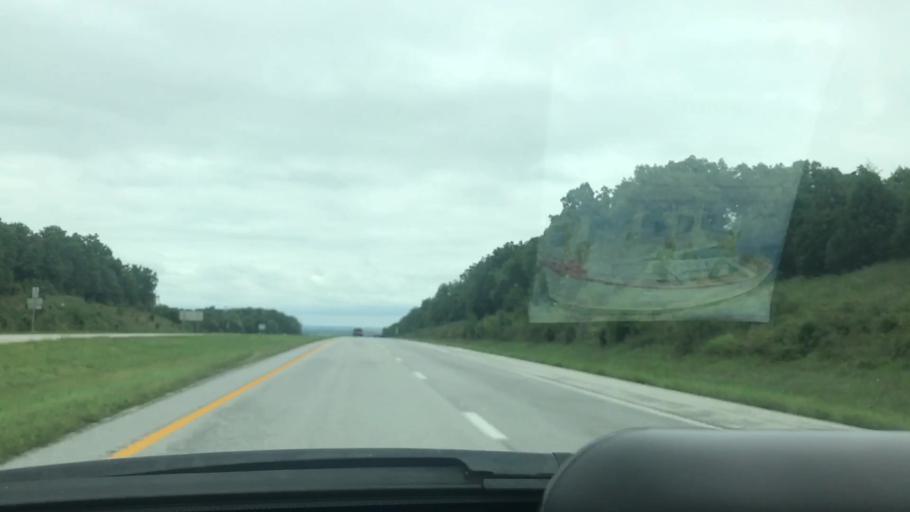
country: US
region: Missouri
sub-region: Greene County
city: Fair Grove
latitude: 37.3295
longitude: -93.1680
